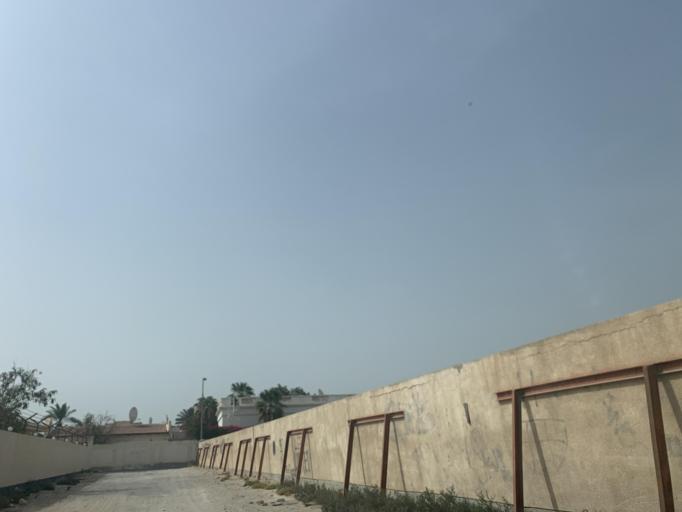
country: BH
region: Manama
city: Jidd Hafs
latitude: 26.2033
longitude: 50.4812
